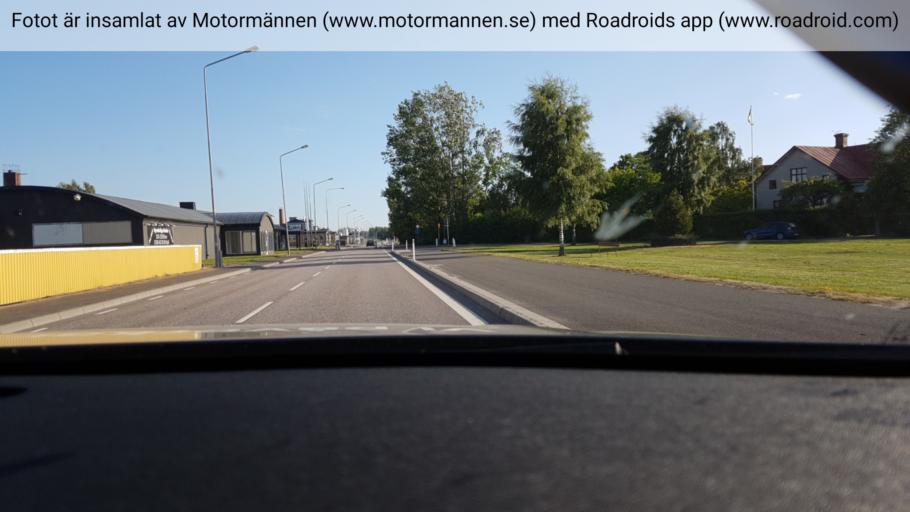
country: SE
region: Vaestra Goetaland
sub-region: Toreboda Kommun
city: Toereboda
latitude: 58.7014
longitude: 14.1222
